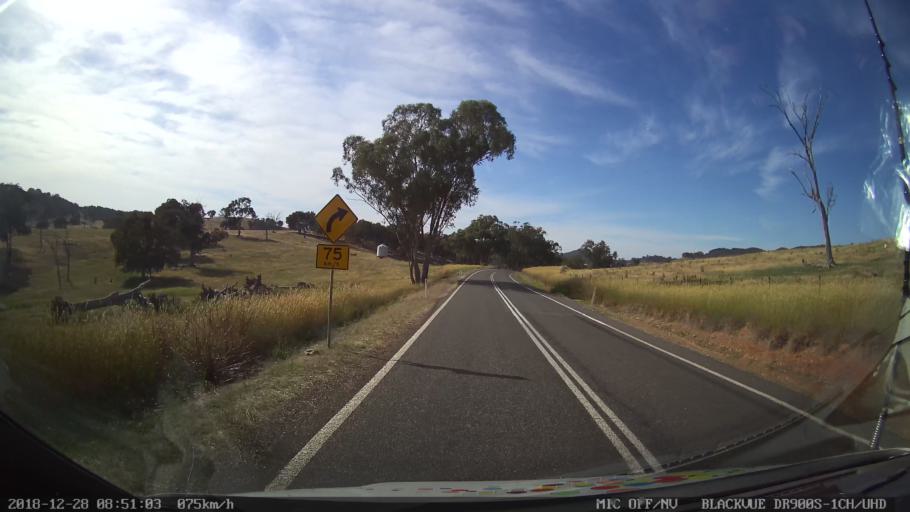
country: AU
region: New South Wales
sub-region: Upper Lachlan Shire
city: Crookwell
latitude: -34.0638
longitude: 149.3392
